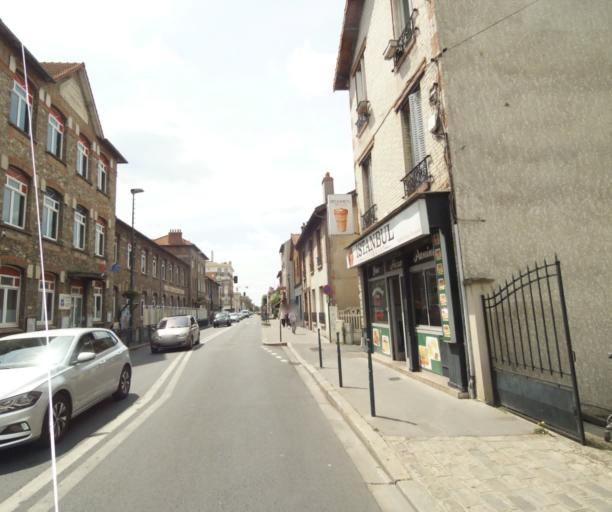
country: FR
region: Ile-de-France
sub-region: Departement des Hauts-de-Seine
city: Colombes
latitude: 48.9180
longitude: 2.2384
